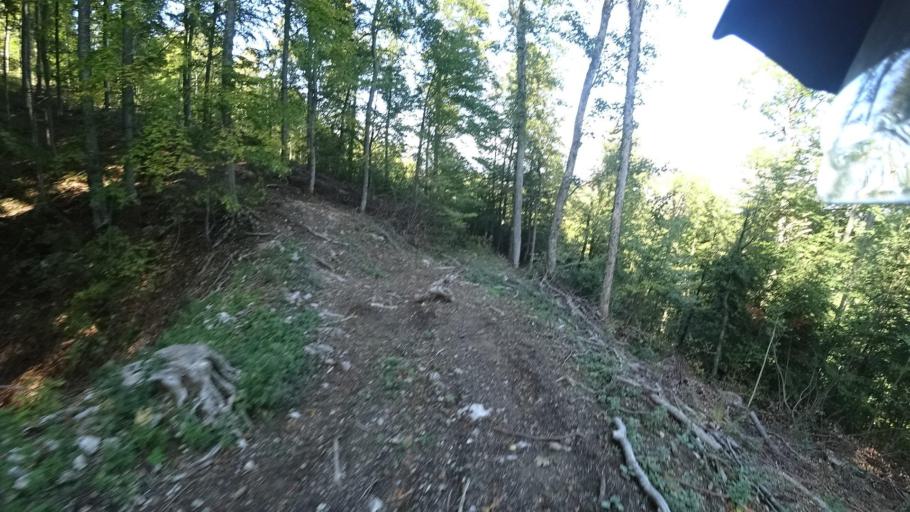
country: HR
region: Primorsko-Goranska
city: Vrbovsko
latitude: 45.2986
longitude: 15.1308
